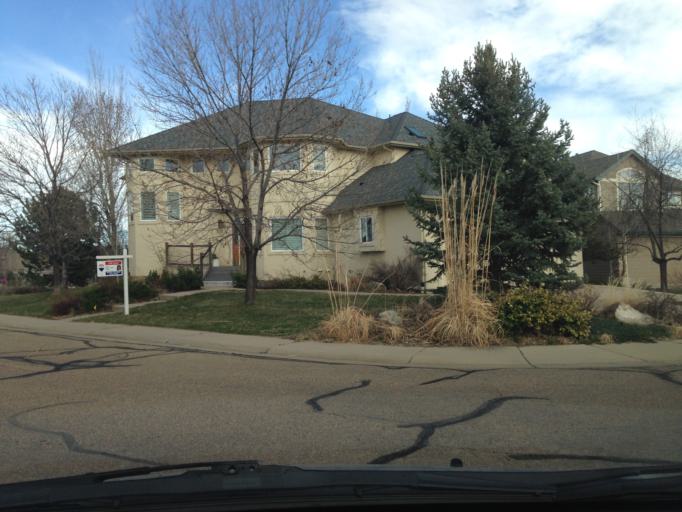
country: US
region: Colorado
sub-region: Boulder County
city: Louisville
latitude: 39.9961
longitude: -105.1175
